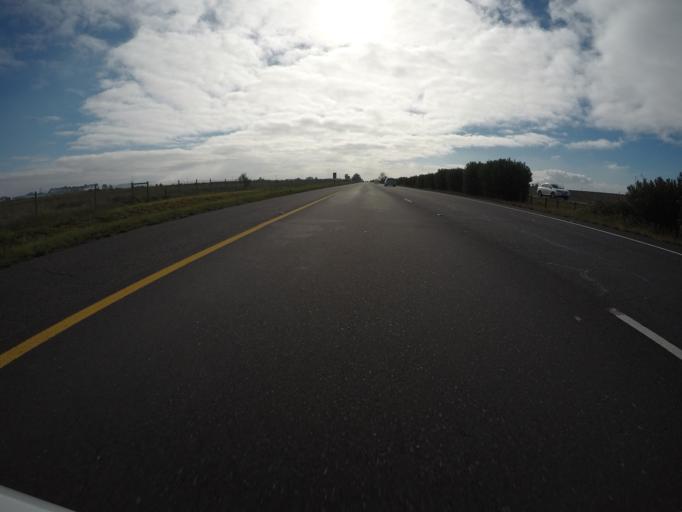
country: ZA
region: Western Cape
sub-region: City of Cape Town
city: Kraaifontein
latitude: -33.8296
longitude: 18.7562
